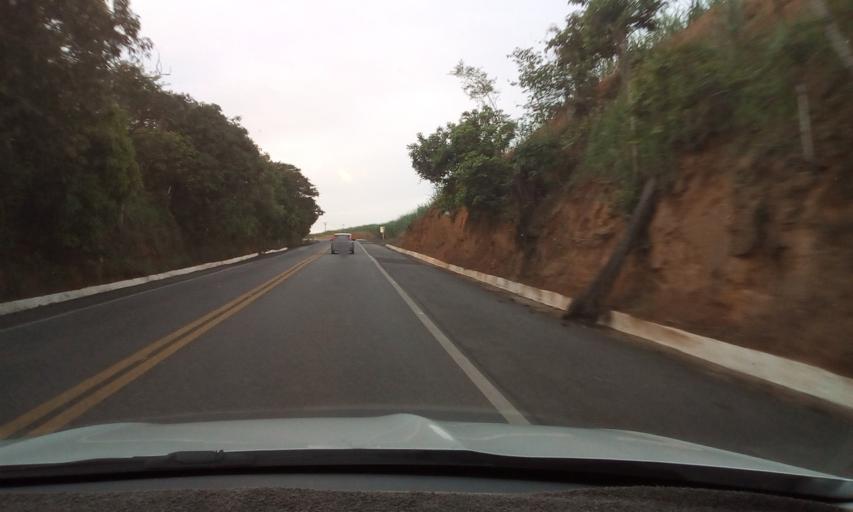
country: BR
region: Pernambuco
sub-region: Vicencia
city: Vicencia
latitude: -7.6117
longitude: -35.2397
